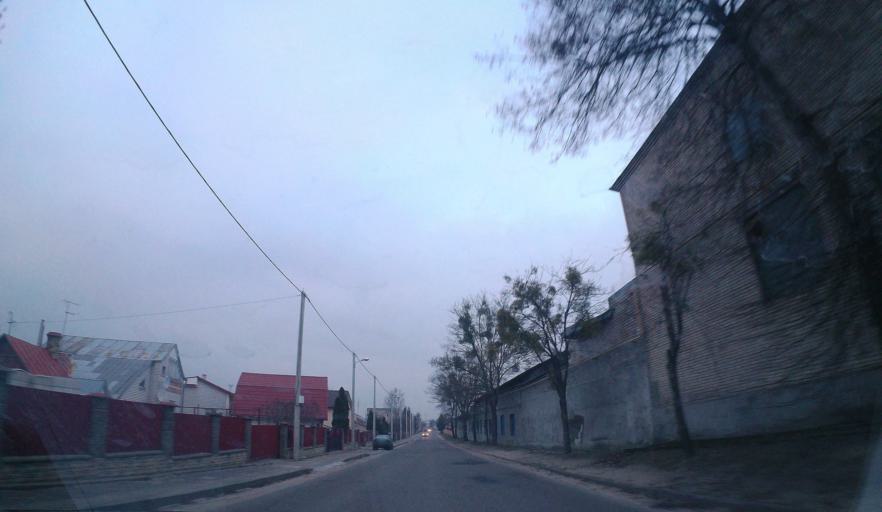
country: BY
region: Grodnenskaya
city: Hrodna
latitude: 53.6550
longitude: 23.8090
